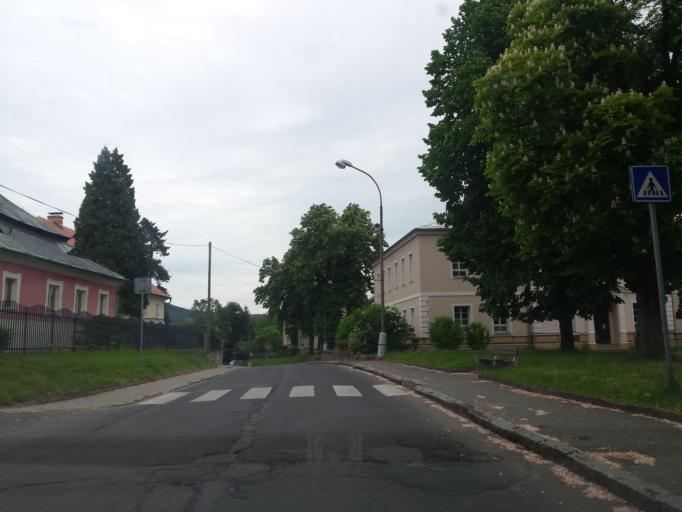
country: CZ
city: Novy Bor
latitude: 50.7395
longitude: 14.5884
